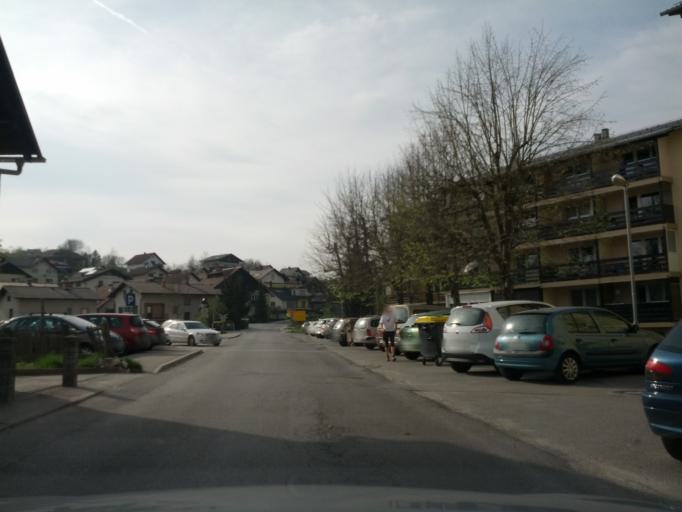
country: SI
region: Kamnik
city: Kamnik
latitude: 46.2293
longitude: 14.6104
